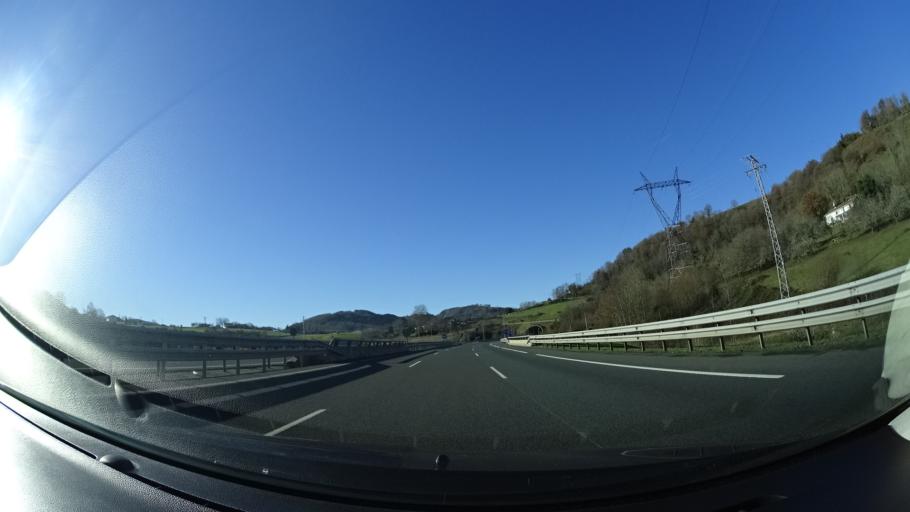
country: ES
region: Basque Country
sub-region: Provincia de Guipuzcoa
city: Errenteria
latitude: 43.2855
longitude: -1.9077
